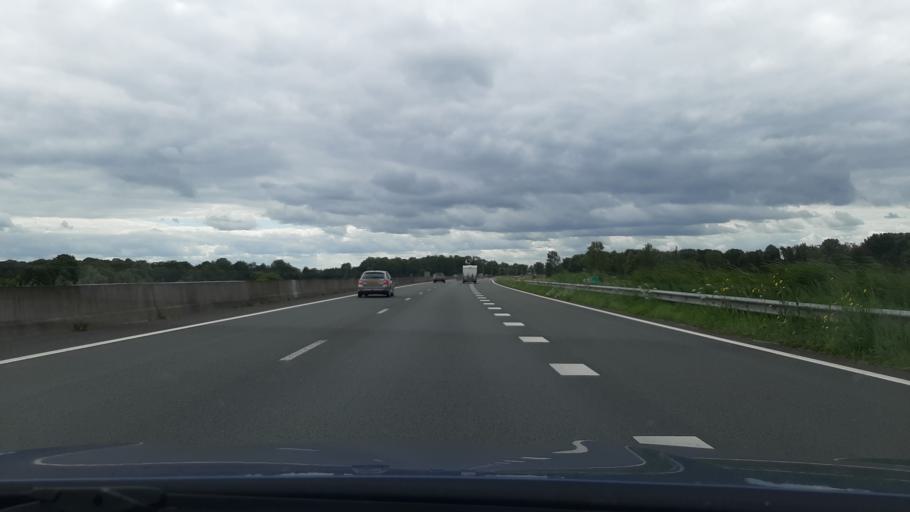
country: NL
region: Groningen
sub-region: Gemeente Haren
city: Haren
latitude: 53.1458
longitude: 6.6065
